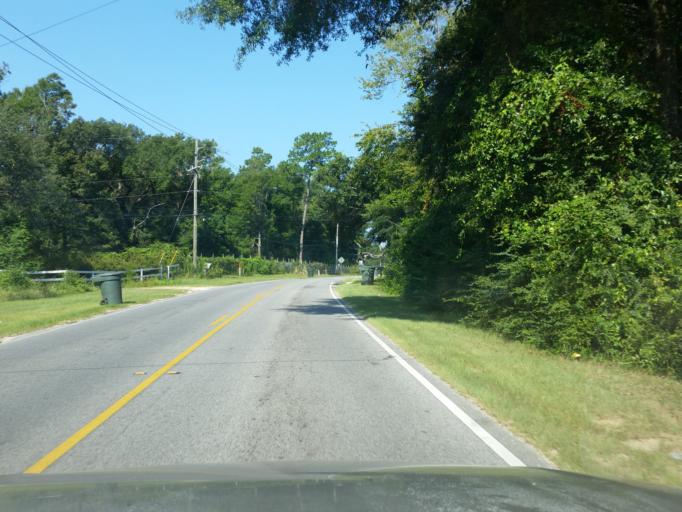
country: US
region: Florida
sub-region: Escambia County
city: Ensley
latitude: 30.5174
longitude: -87.2443
